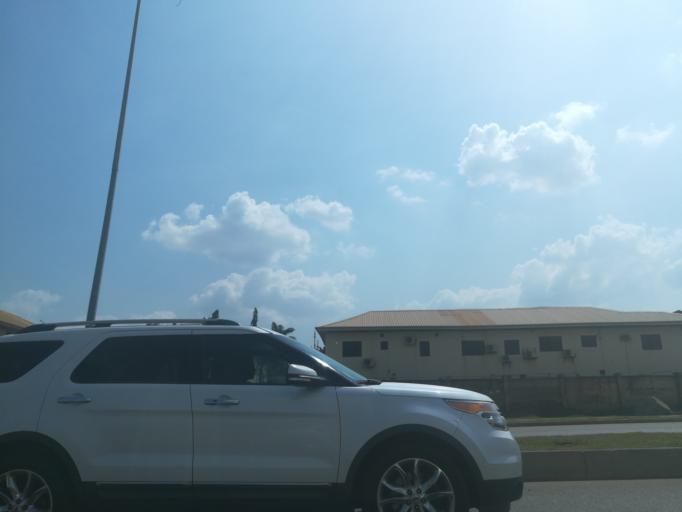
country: NG
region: Abuja Federal Capital Territory
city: Abuja
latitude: 9.0529
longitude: 7.4474
